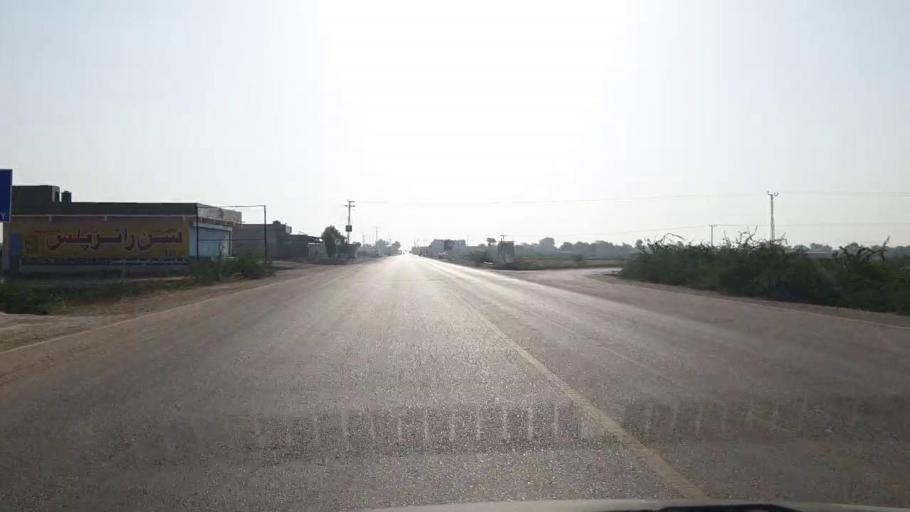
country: PK
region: Sindh
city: Badin
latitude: 24.6781
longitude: 68.8454
